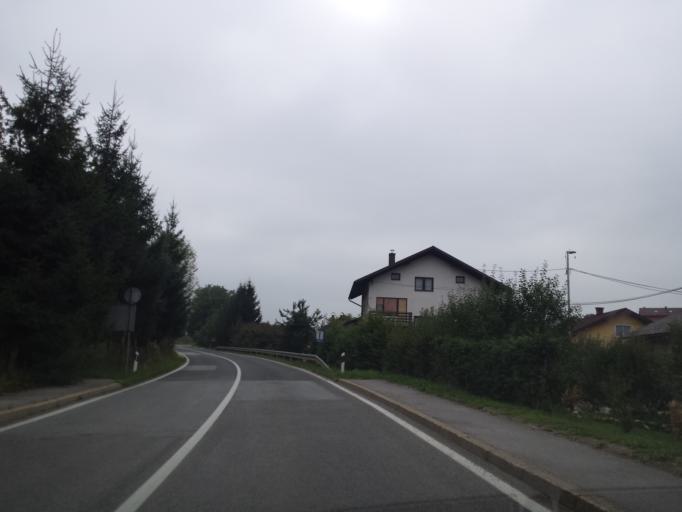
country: HR
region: Karlovacka
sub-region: Grad Karlovac
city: Karlovac
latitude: 45.4518
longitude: 15.4919
